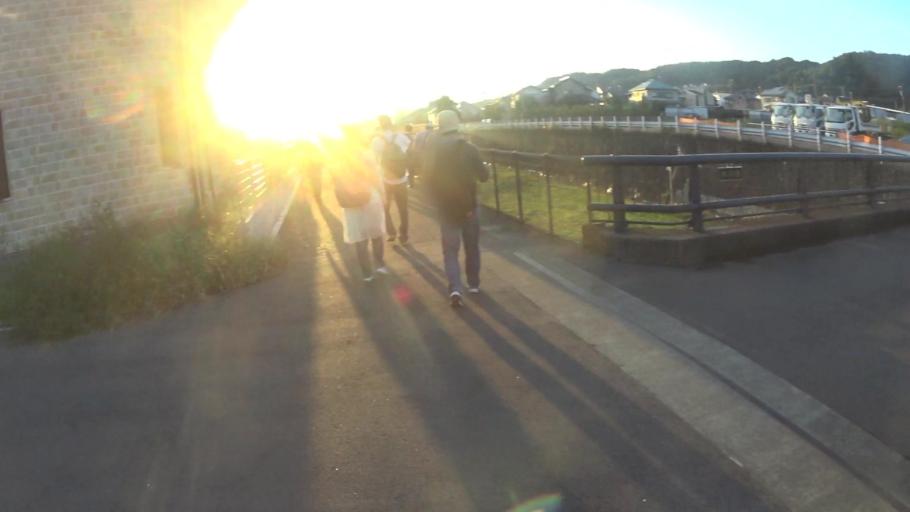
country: JP
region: Tokyo
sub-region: Machida-shi
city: Machida
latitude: 35.5861
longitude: 139.4451
